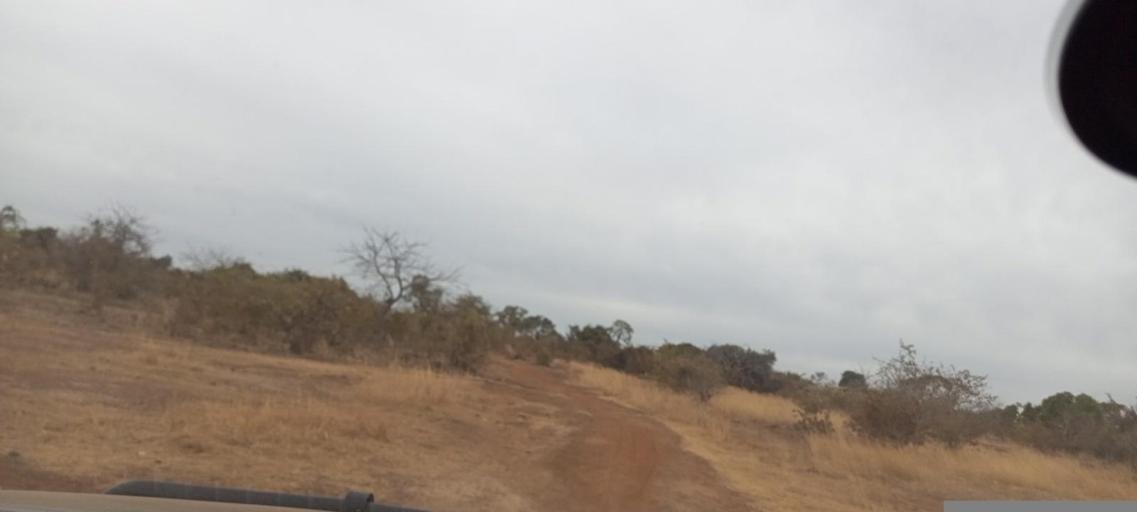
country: ML
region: Koulikoro
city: Kati
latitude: 12.7607
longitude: -8.2843
